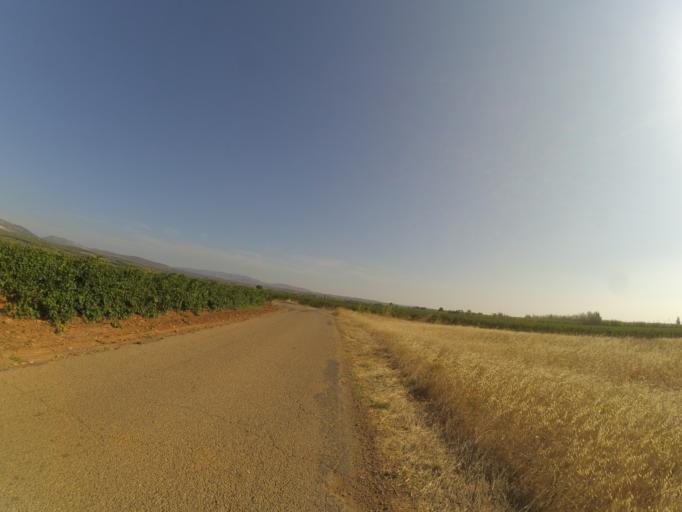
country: FR
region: Languedoc-Roussillon
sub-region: Departement des Pyrenees-Orientales
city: Rivesaltes
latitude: 42.7894
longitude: 2.8462
